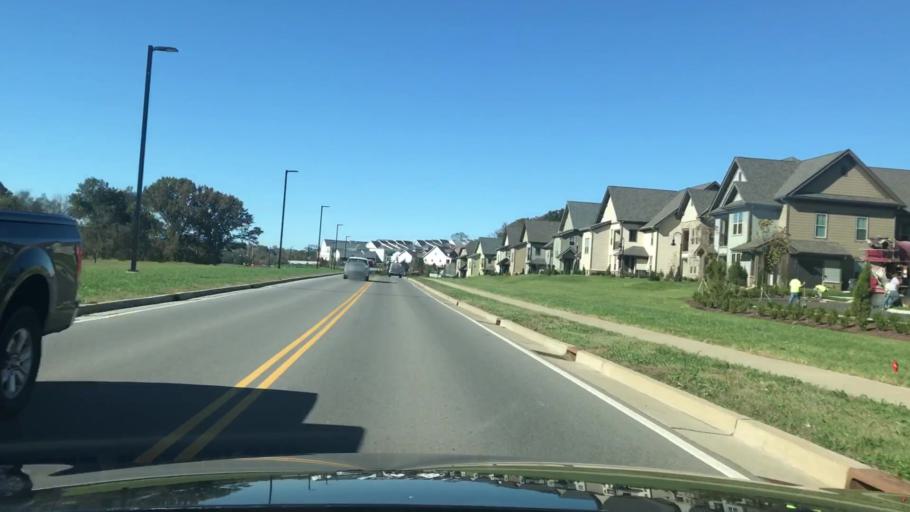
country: US
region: Tennessee
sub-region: Williamson County
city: Franklin
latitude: 35.8876
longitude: -86.8197
